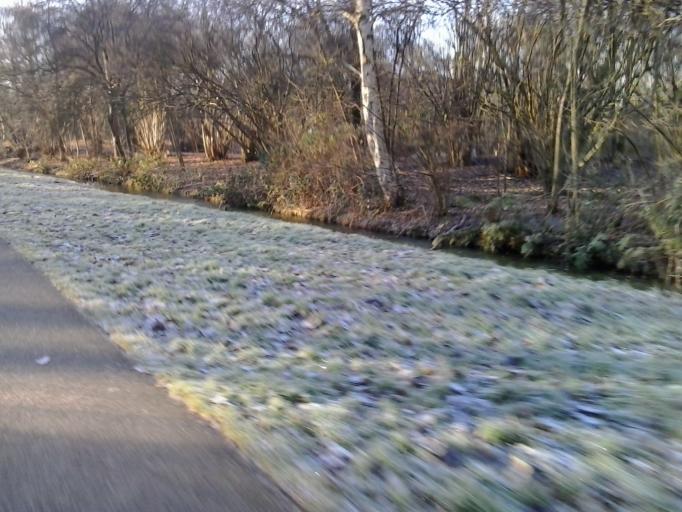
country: NL
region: South Holland
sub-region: Gemeente Lansingerland
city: Bergschenhoek
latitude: 51.9657
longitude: 4.5128
